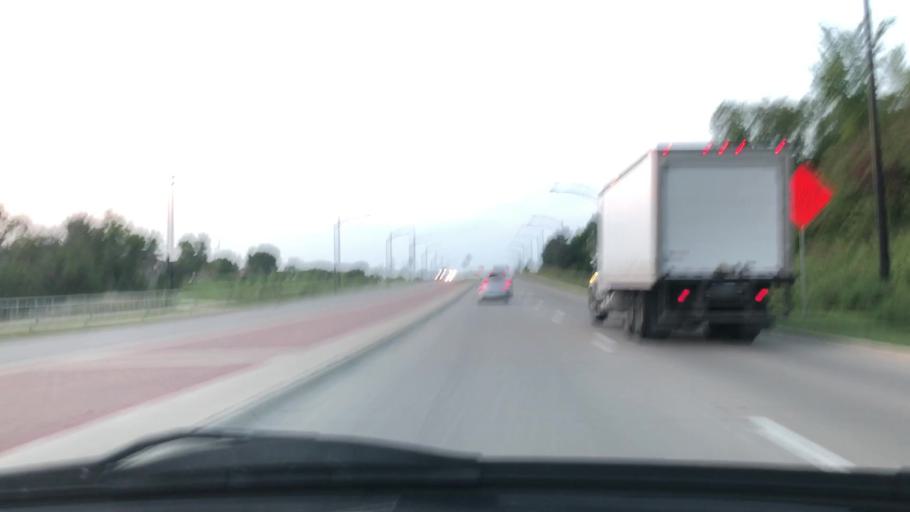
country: US
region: Iowa
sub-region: Johnson County
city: Coralville
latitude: 41.7039
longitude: -91.6081
